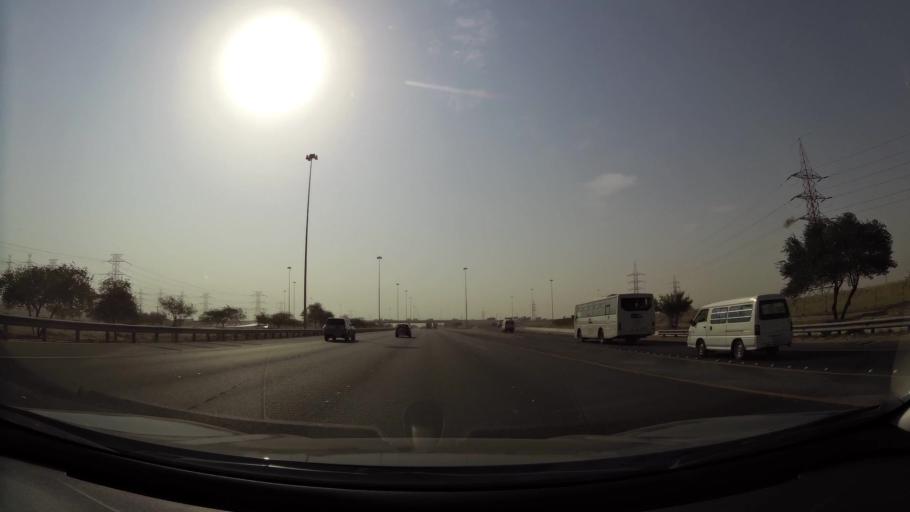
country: KW
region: Al Ahmadi
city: Al Ahmadi
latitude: 28.9949
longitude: 48.0998
